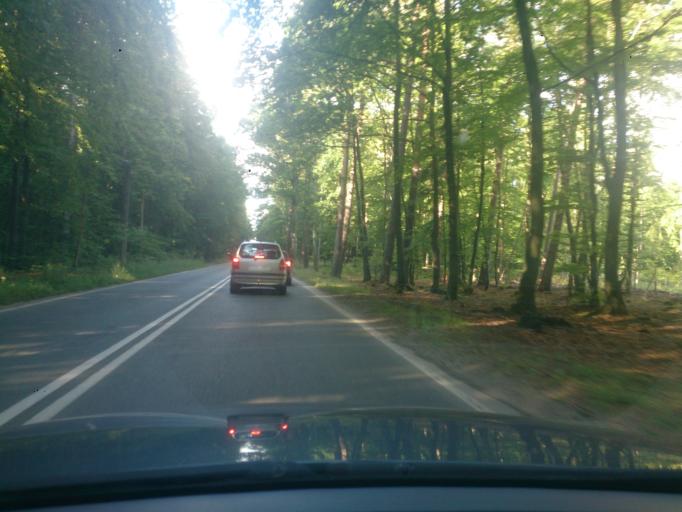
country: PL
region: Pomeranian Voivodeship
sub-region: Gdynia
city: Wielki Kack
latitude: 54.4620
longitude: 18.5087
